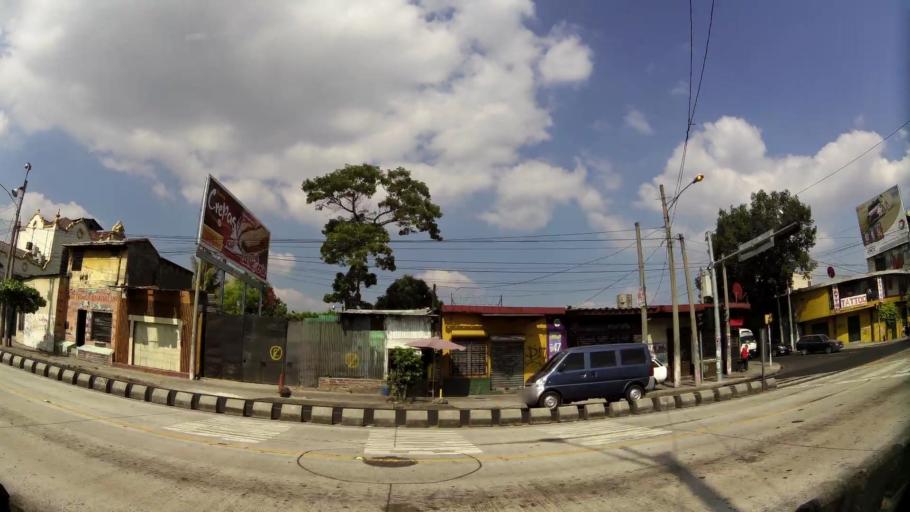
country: SV
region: San Salvador
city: San Salvador
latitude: 13.7003
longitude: -89.1887
